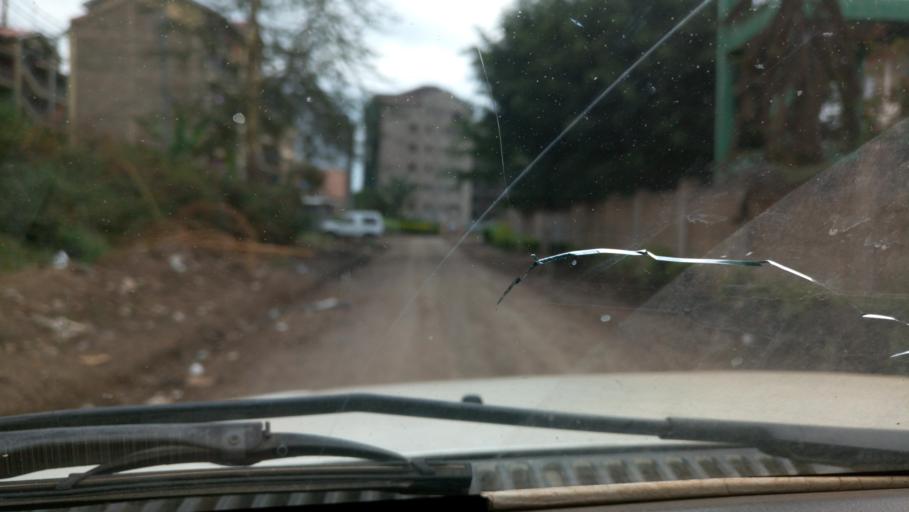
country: KE
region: Nairobi Area
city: Pumwani
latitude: -1.3217
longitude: 36.8453
